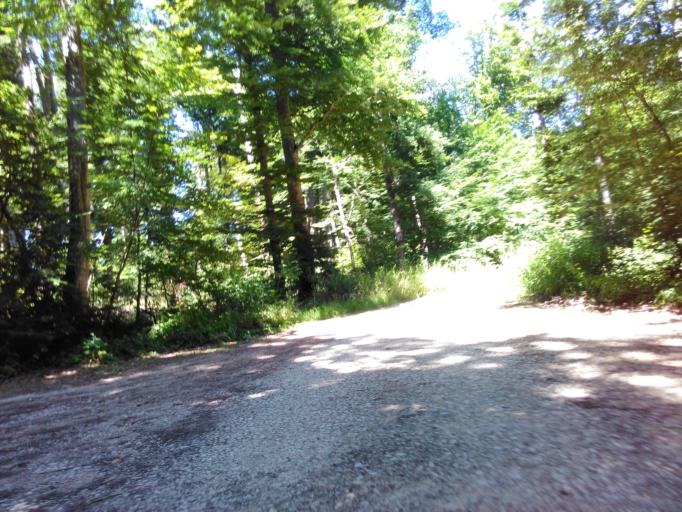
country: LU
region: Luxembourg
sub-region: Canton d'Esch-sur-Alzette
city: Leudelange
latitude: 49.5425
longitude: 6.0736
